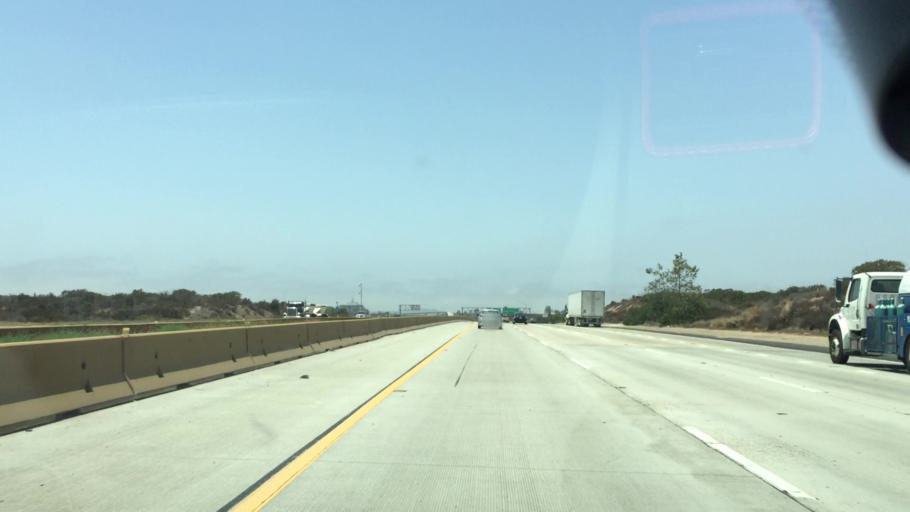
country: US
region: California
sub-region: San Diego County
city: La Mesa
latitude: 32.8419
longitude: -117.1092
